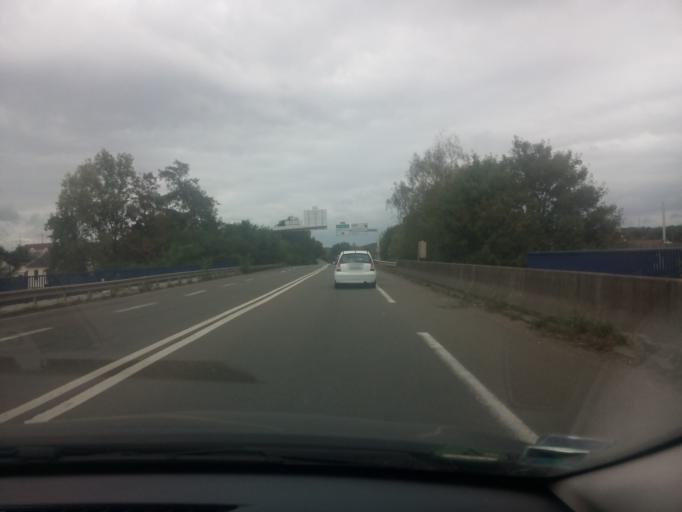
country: FR
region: Ile-de-France
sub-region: Departement de l'Essonne
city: Palaiseau
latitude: 48.7261
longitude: 2.2447
